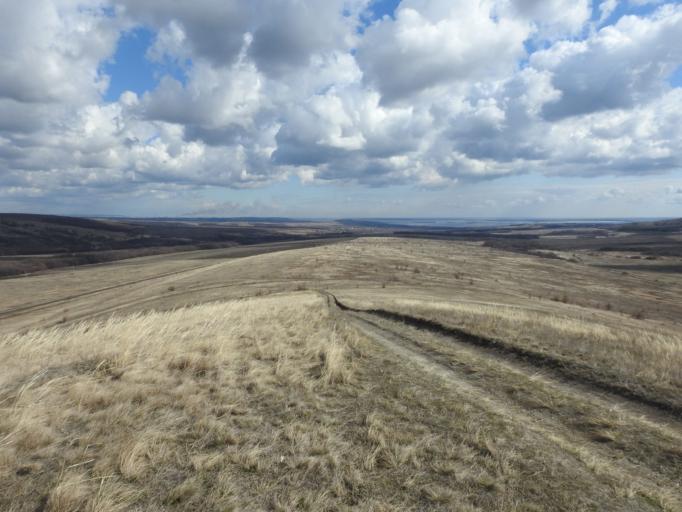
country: RU
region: Saratov
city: Krasnyy Oktyabr'
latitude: 51.3756
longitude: 45.7582
